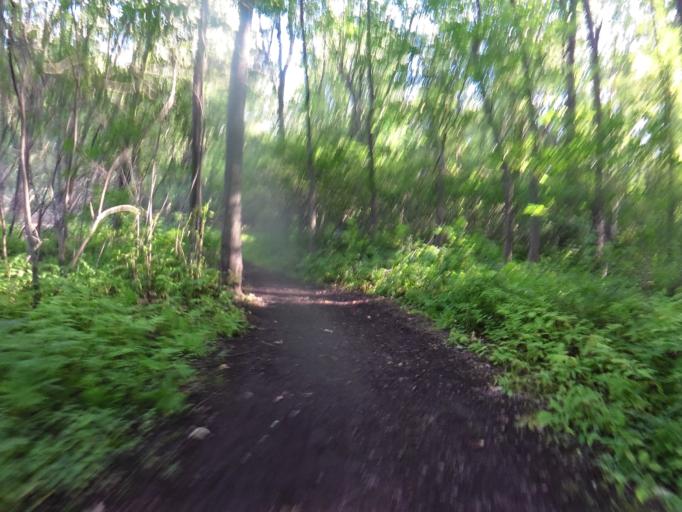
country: CA
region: Quebec
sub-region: Outaouais
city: Gatineau
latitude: 45.4811
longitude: -75.5894
